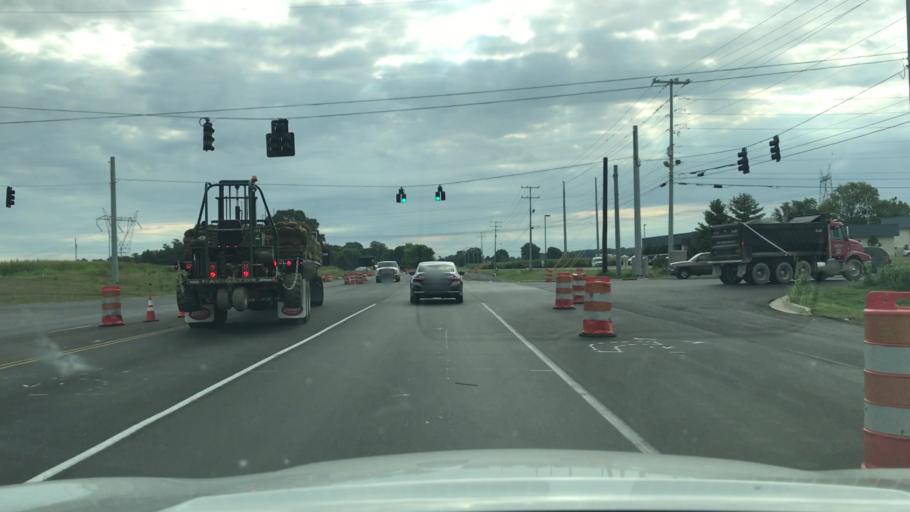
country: US
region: Kentucky
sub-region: Todd County
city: Guthrie
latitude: 36.6093
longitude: -87.2588
